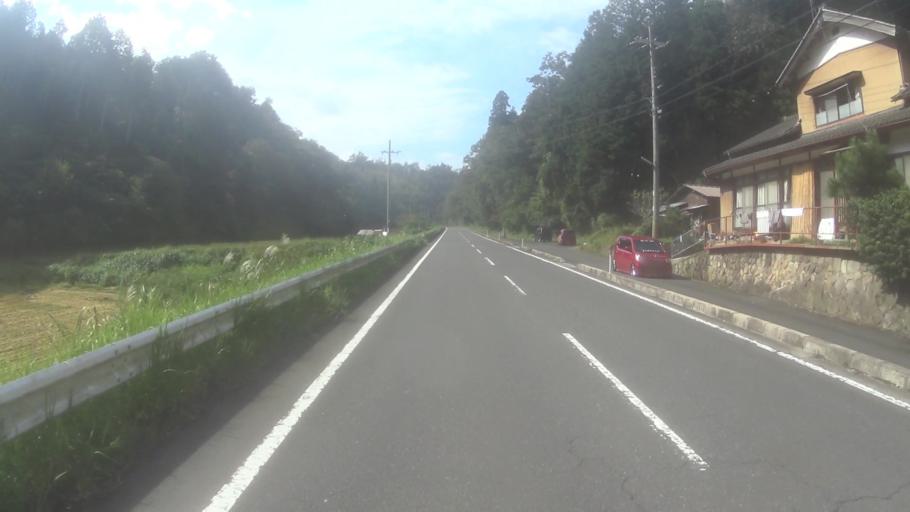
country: JP
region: Kyoto
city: Miyazu
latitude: 35.5905
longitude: 135.1299
